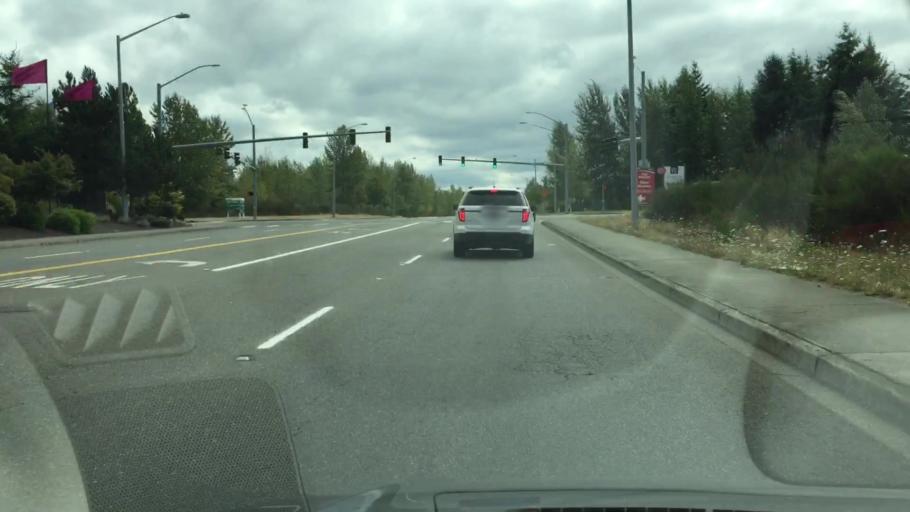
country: US
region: Washington
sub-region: Pierce County
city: South Hill
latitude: 47.0987
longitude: -122.2655
